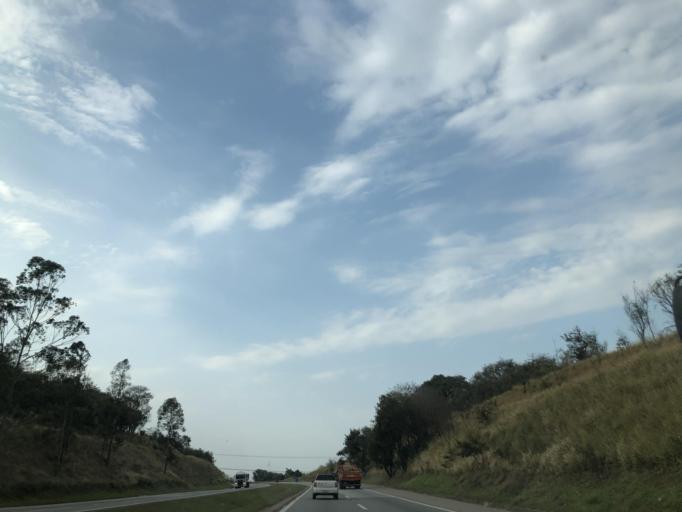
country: BR
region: Sao Paulo
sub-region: Sorocaba
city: Sorocaba
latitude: -23.4640
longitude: -47.3811
